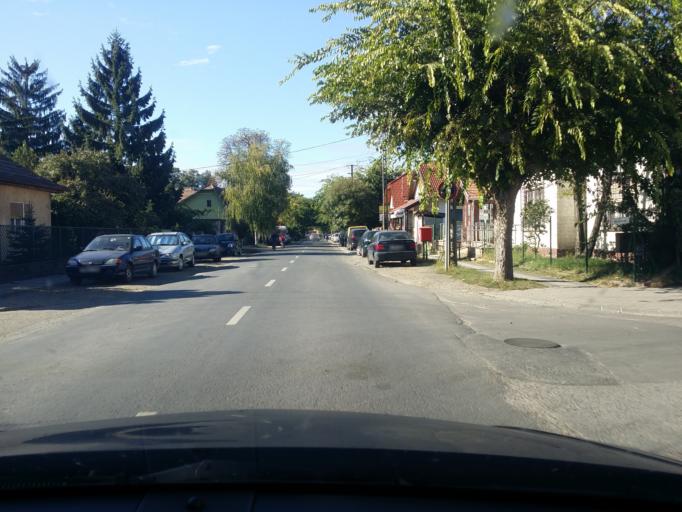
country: HU
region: Pest
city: God
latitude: 47.7028
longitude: 19.1472
